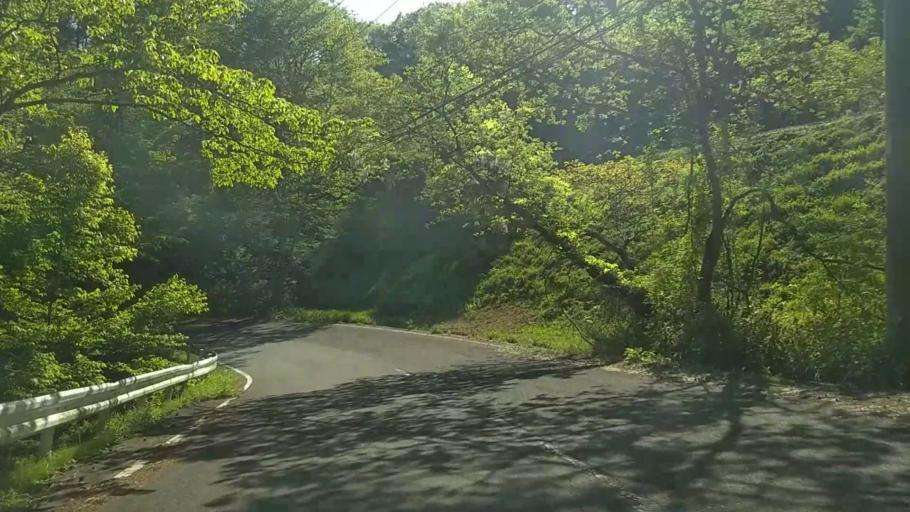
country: JP
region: Yamanashi
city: Nirasaki
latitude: 35.8891
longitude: 138.3902
